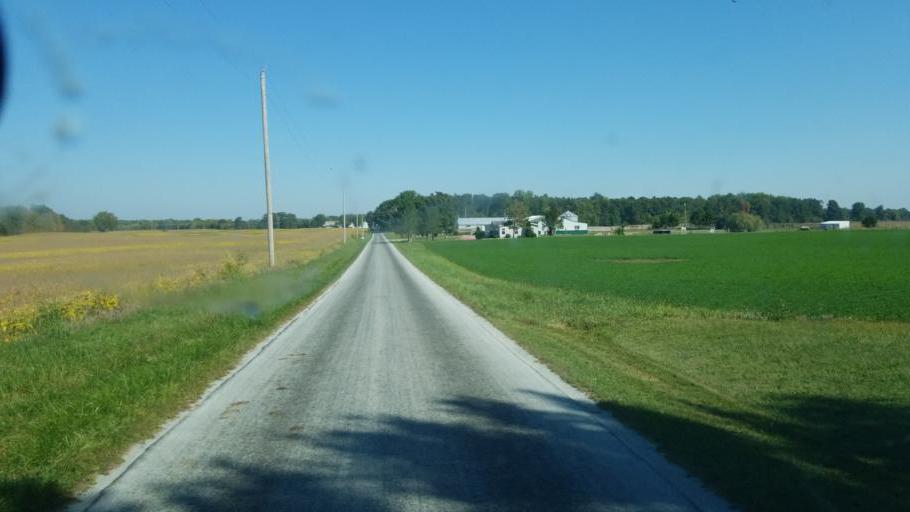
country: US
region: Ohio
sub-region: Hardin County
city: Kenton
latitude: 40.5761
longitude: -83.4880
